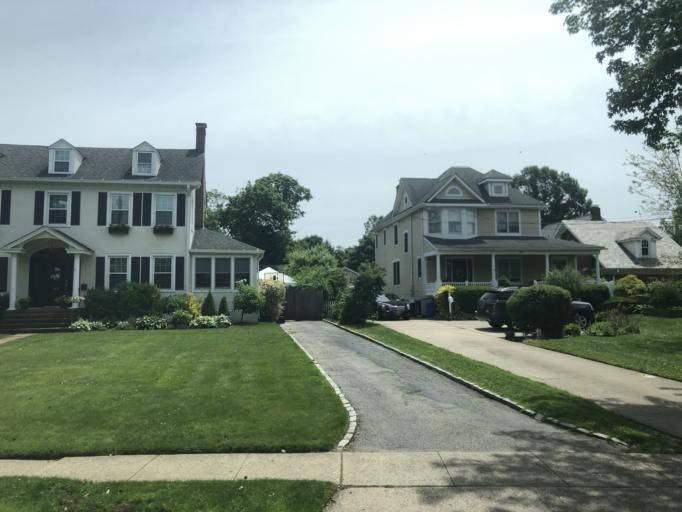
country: US
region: New York
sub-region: Nassau County
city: Rockville Centre
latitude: 40.6651
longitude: -73.6431
